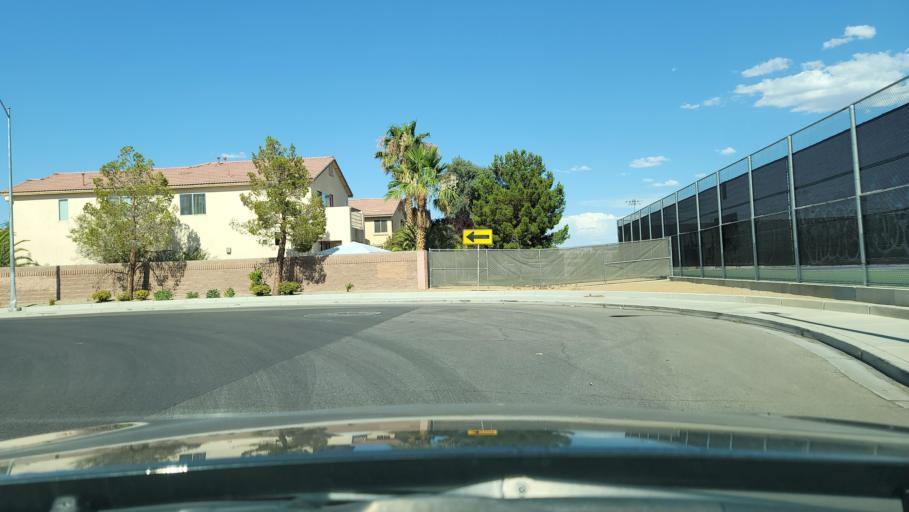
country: US
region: Nevada
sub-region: Clark County
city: Spring Valley
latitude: 36.0905
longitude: -115.2477
